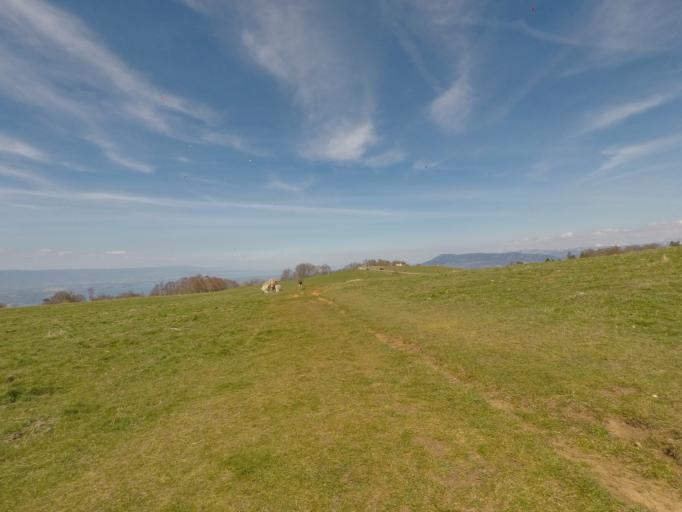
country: FR
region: Rhone-Alpes
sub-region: Departement de la Haute-Savoie
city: Collonges-sous-Saleve
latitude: 46.1370
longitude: 6.1776
